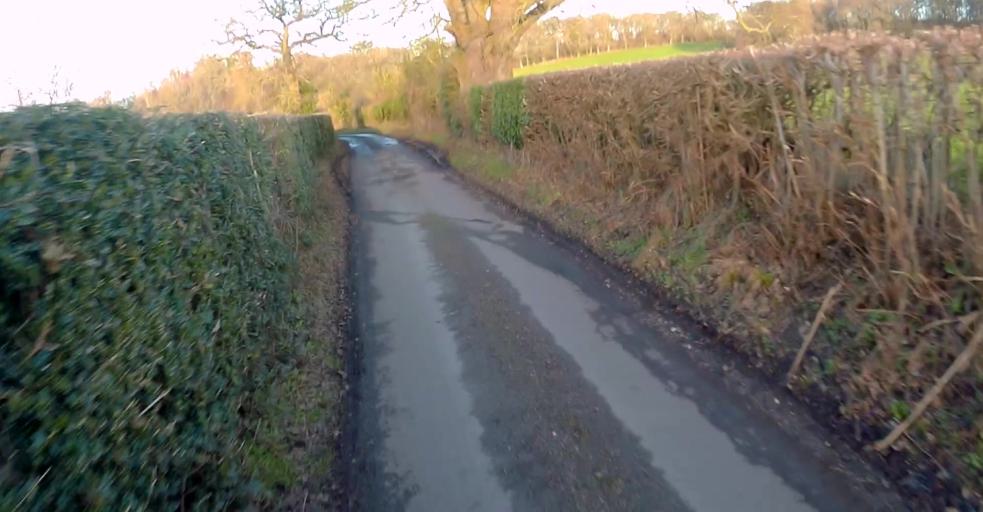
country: GB
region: England
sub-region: Hampshire
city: Hook
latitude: 51.3216
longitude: -0.9972
